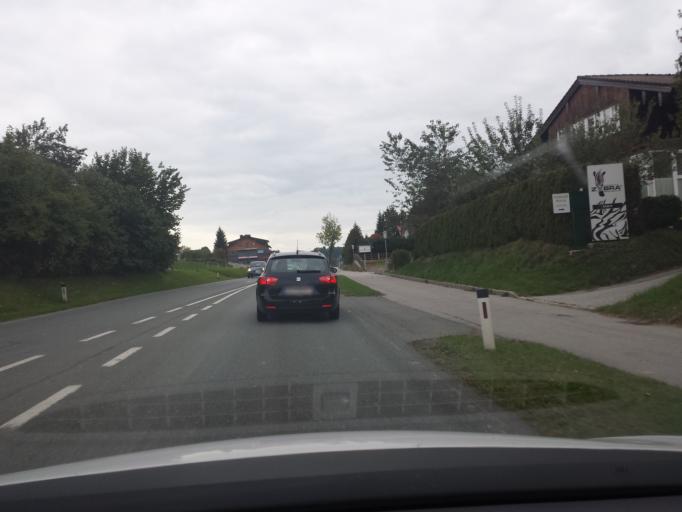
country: AT
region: Salzburg
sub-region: Politischer Bezirk Salzburg-Umgebung
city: Hof bei Salzburg
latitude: 47.8194
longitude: 13.2120
